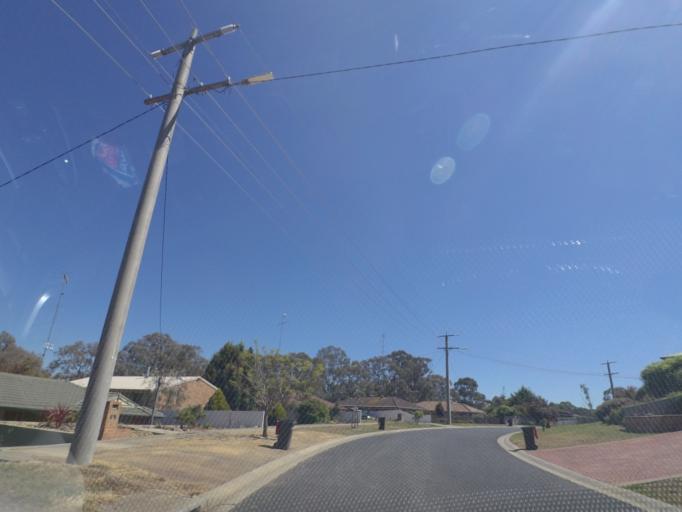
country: AU
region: Victoria
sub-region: Whittlesea
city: Whittlesea
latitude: -37.2086
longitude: 145.0616
